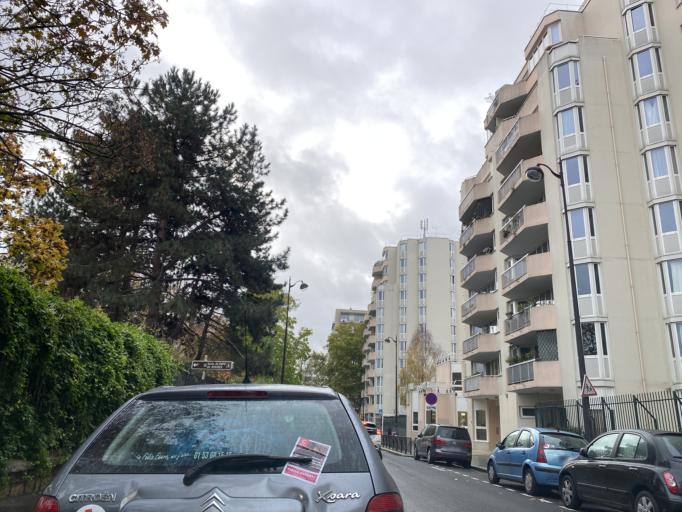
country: FR
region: Ile-de-France
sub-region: Departement de Seine-Saint-Denis
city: Le Pre-Saint-Gervais
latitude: 48.8598
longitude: 2.3837
